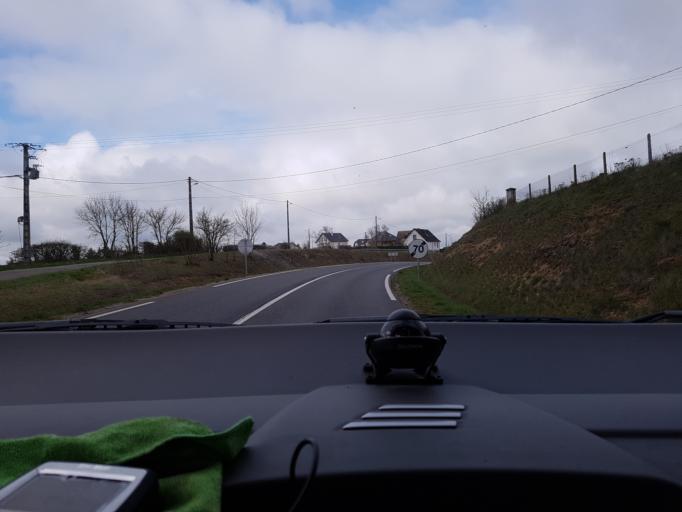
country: FR
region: Midi-Pyrenees
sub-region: Departement de l'Aveyron
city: Olemps
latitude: 44.3690
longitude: 2.5339
